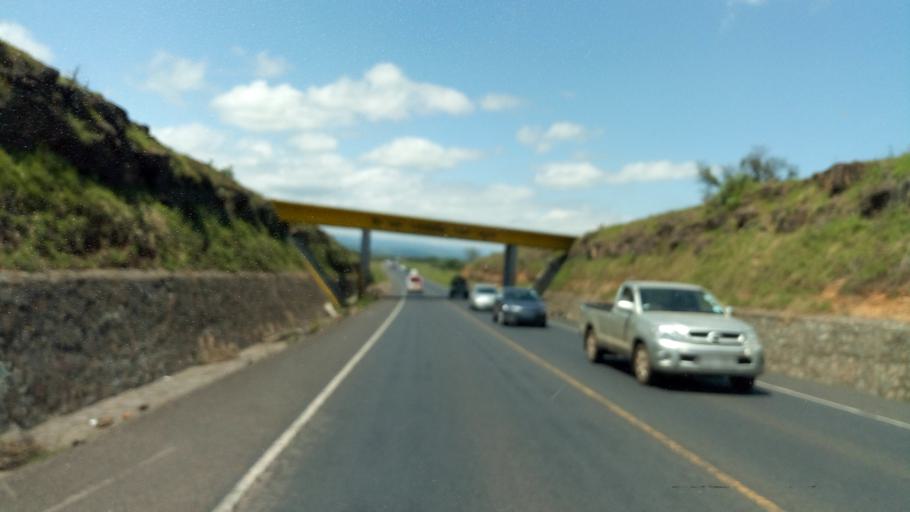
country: KE
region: Nakuru
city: Naivasha
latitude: -0.5433
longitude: 36.3401
